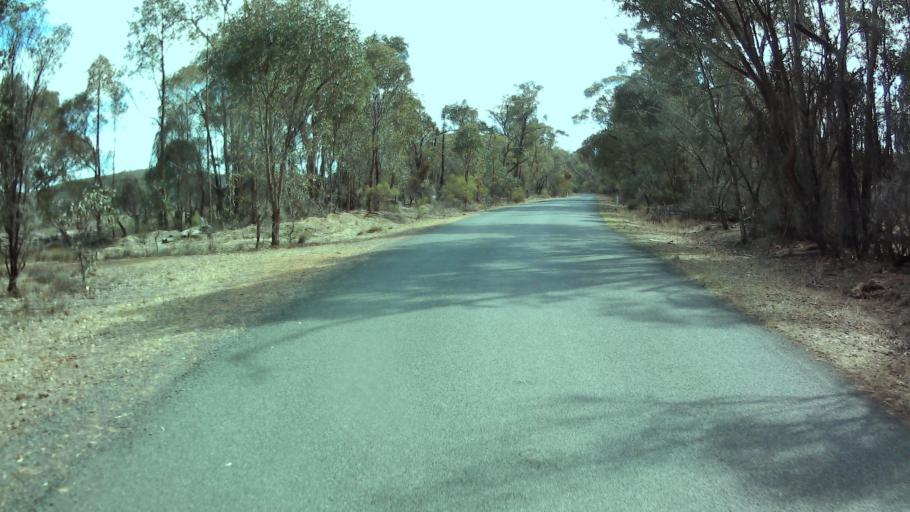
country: AU
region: New South Wales
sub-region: Weddin
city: Grenfell
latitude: -33.8716
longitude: 148.2026
